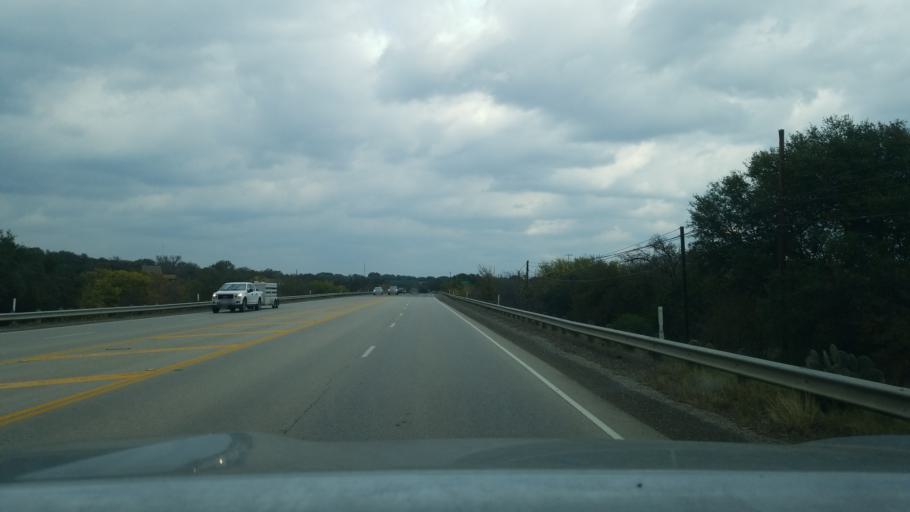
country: US
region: Texas
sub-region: Blanco County
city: Johnson City
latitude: 30.2900
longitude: -98.4023
